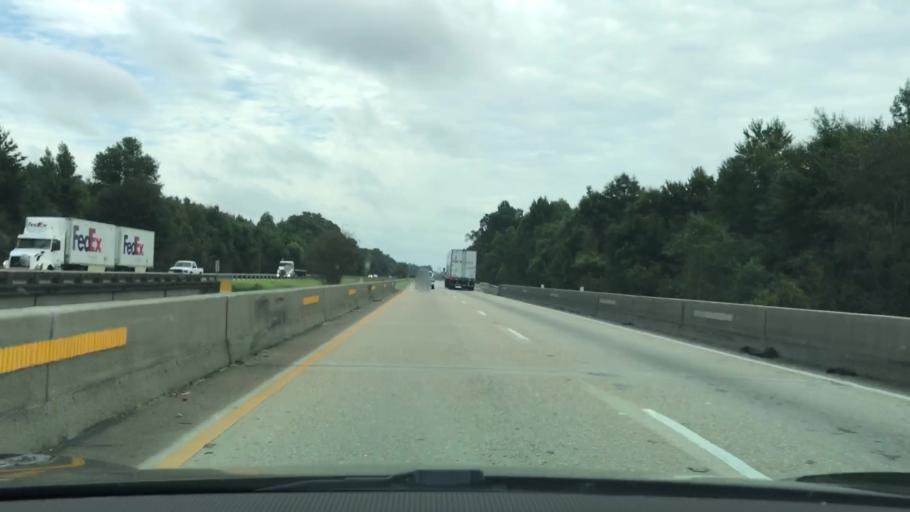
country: US
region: Alabama
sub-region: Elmore County
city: Tallassee
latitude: 32.3954
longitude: -85.9796
